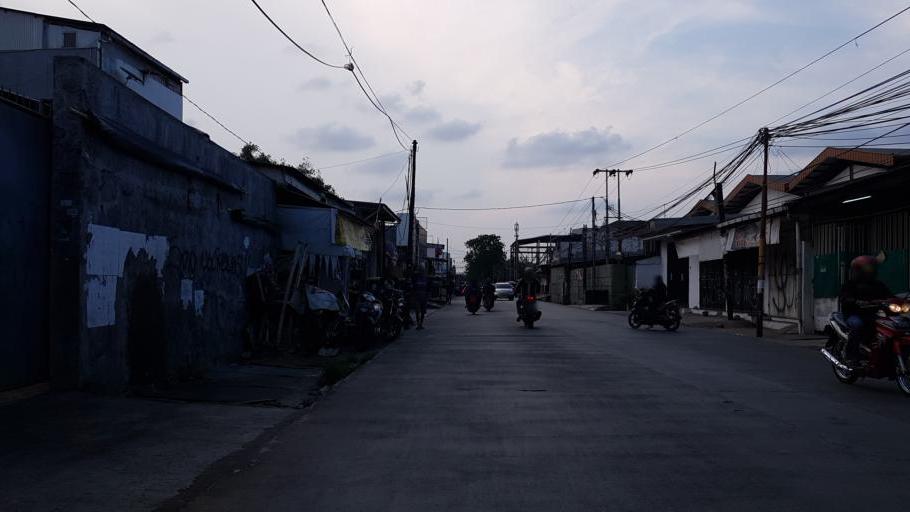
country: ID
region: Jakarta Raya
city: Jakarta
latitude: -6.1371
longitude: 106.7576
